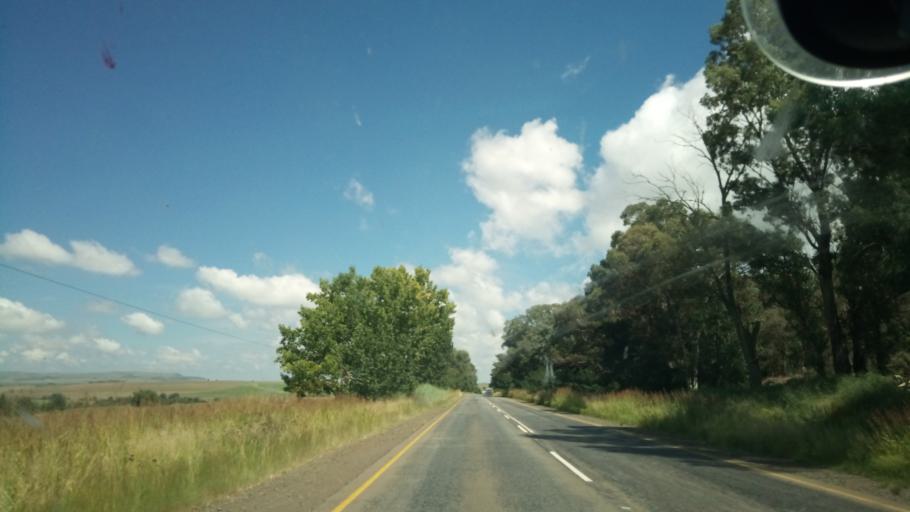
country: ZA
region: Orange Free State
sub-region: Thabo Mofutsanyana District Municipality
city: Ficksburg
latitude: -28.8957
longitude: 27.7719
